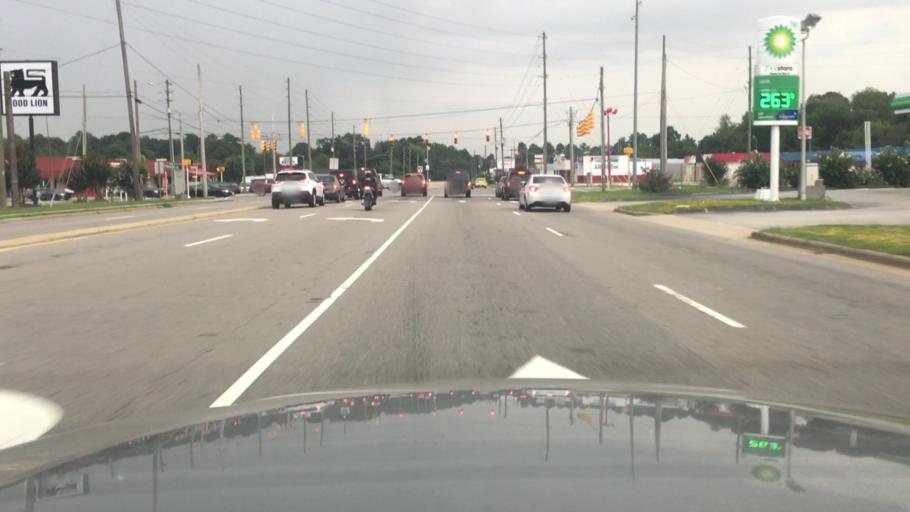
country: US
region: North Carolina
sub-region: Cumberland County
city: Fort Bragg
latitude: 35.0836
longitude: -79.0103
